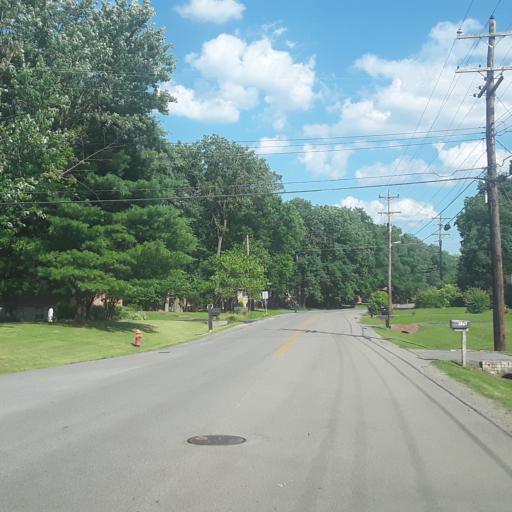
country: US
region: Tennessee
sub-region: Davidson County
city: Lakewood
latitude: 36.2034
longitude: -86.6356
